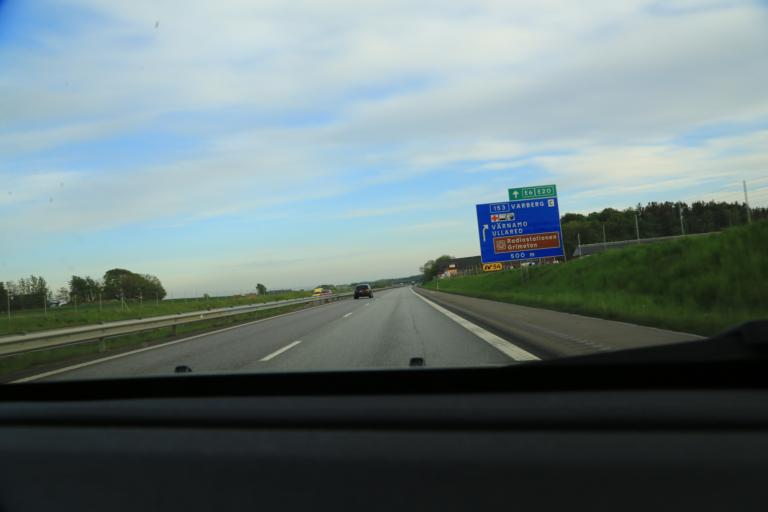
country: SE
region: Halland
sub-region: Varbergs Kommun
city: Varberg
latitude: 57.1348
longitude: 12.3084
